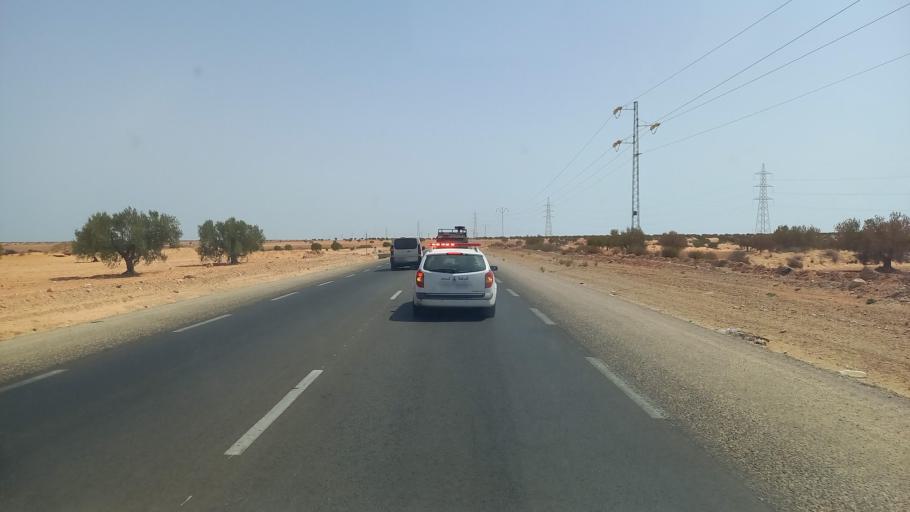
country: TN
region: Madanin
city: Zarzis
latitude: 33.4030
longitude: 10.8475
